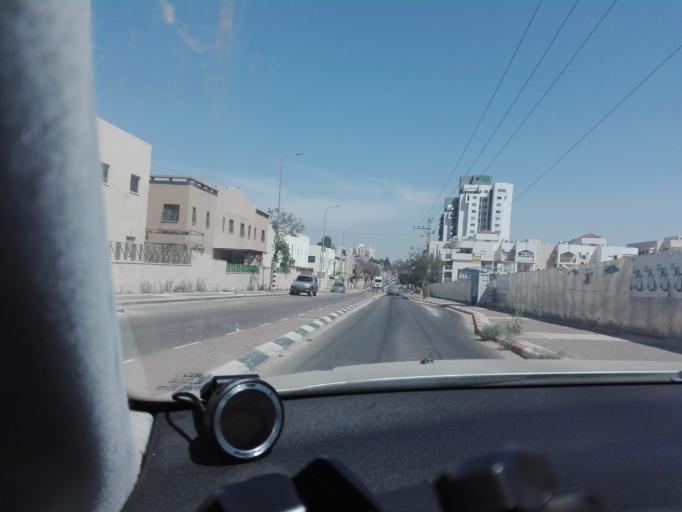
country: IL
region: Central District
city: Bene 'Ayish
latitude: 31.7294
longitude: 34.7373
